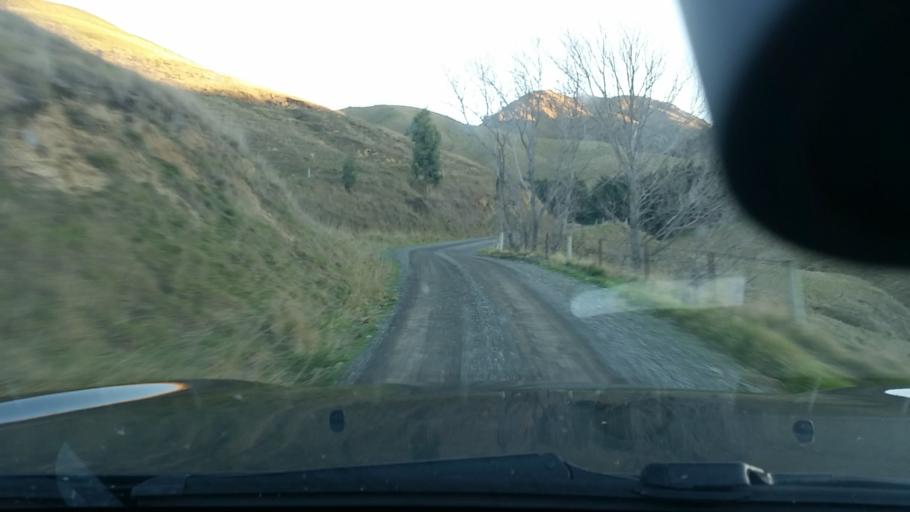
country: NZ
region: Marlborough
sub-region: Marlborough District
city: Blenheim
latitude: -41.7475
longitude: 174.0631
